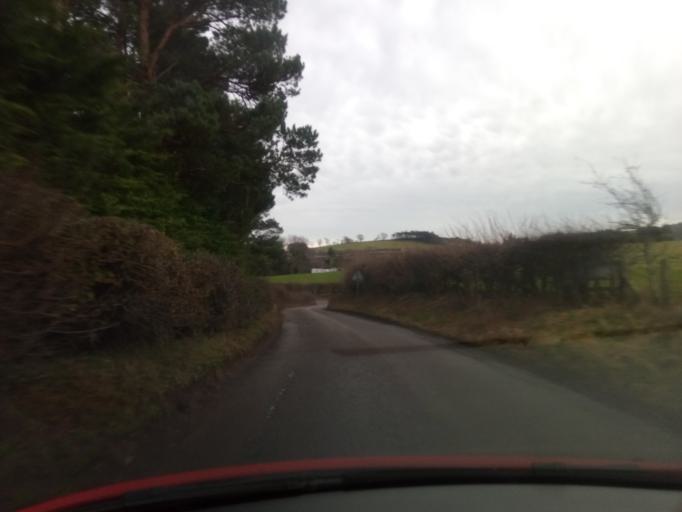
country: GB
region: England
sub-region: Northumberland
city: Wooler
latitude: 55.5502
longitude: -2.0279
